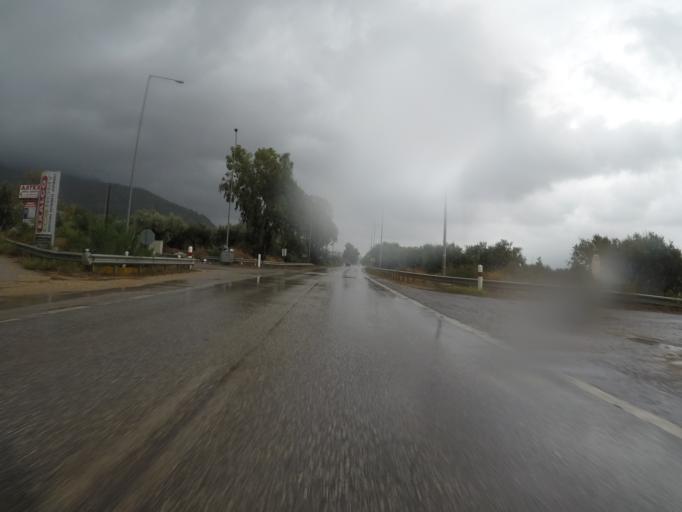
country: GR
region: Peloponnese
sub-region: Nomos Messinias
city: Kyparissia
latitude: 37.2616
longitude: 21.6860
